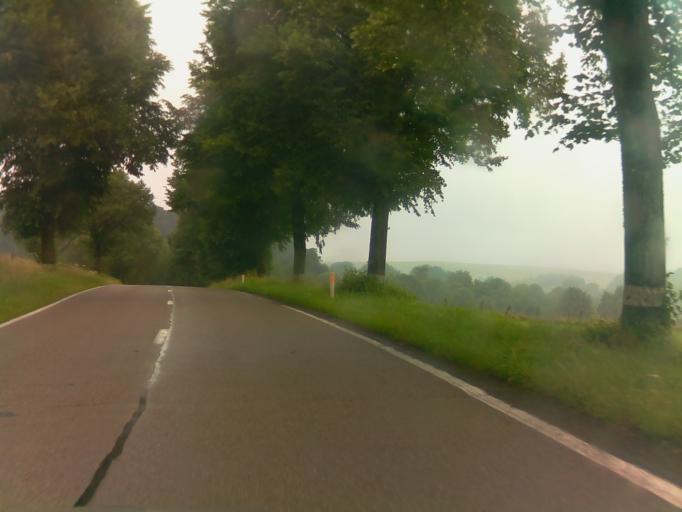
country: BE
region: Wallonia
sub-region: Province du Luxembourg
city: Bertrix
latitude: 49.8423
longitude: 5.3418
